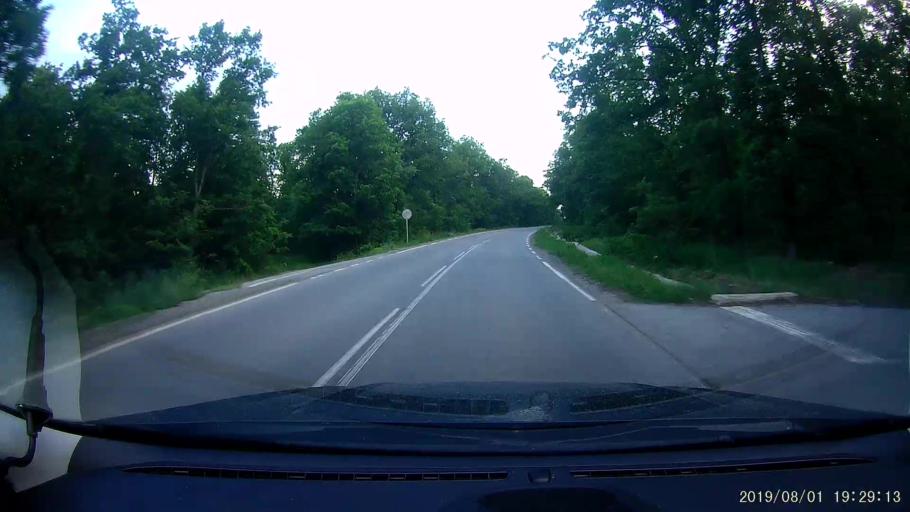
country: BG
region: Burgas
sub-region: Obshtina Sungurlare
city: Sungurlare
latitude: 42.8295
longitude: 26.9095
